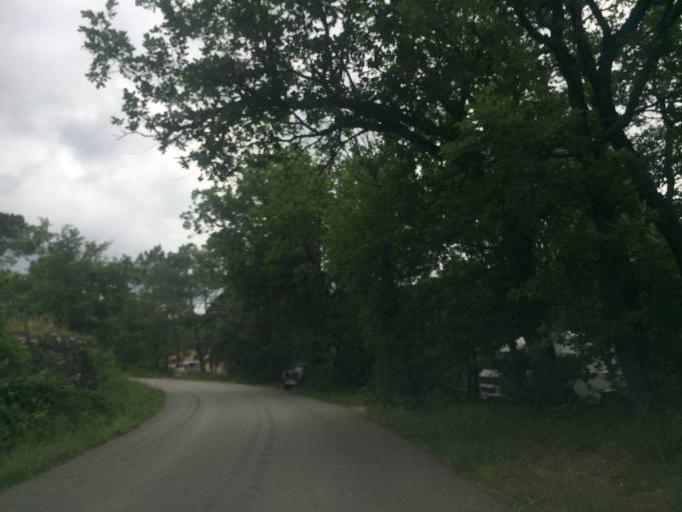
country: FR
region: Rhone-Alpes
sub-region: Departement de l'Ardeche
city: Privas
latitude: 44.7515
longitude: 4.5976
